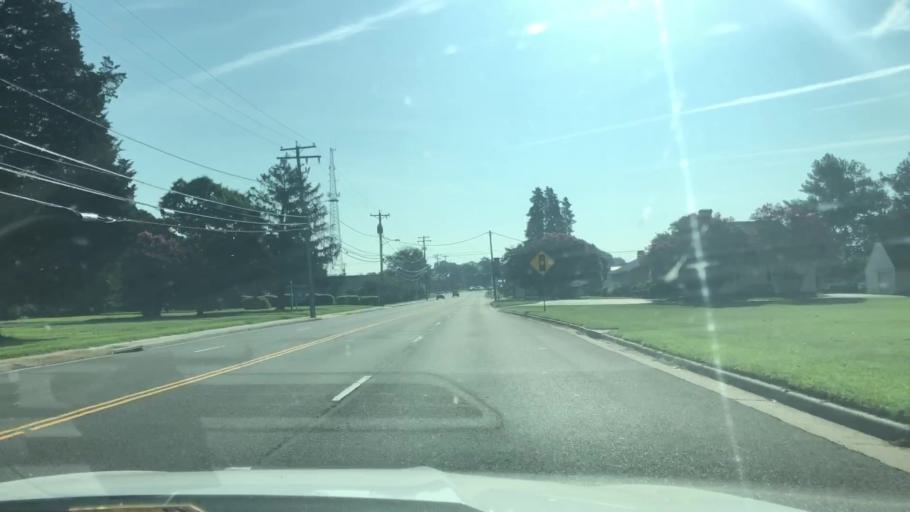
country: US
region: Virginia
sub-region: Richmond County
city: Warsaw
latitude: 37.9586
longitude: -76.7628
